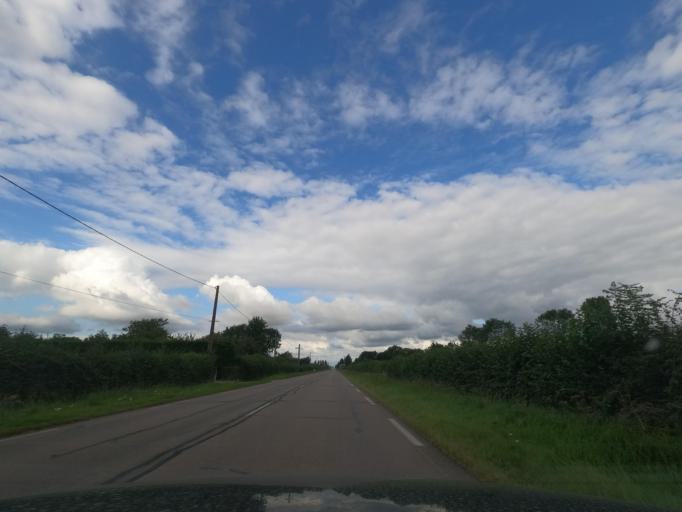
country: FR
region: Lower Normandy
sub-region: Departement du Calvados
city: Orbec
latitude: 48.9073
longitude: 0.4158
